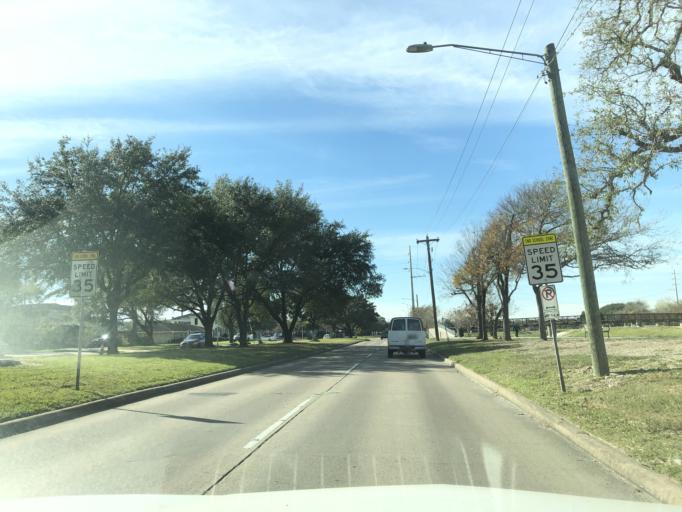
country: US
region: Texas
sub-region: Harris County
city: Bellaire
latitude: 29.6758
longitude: -95.4810
